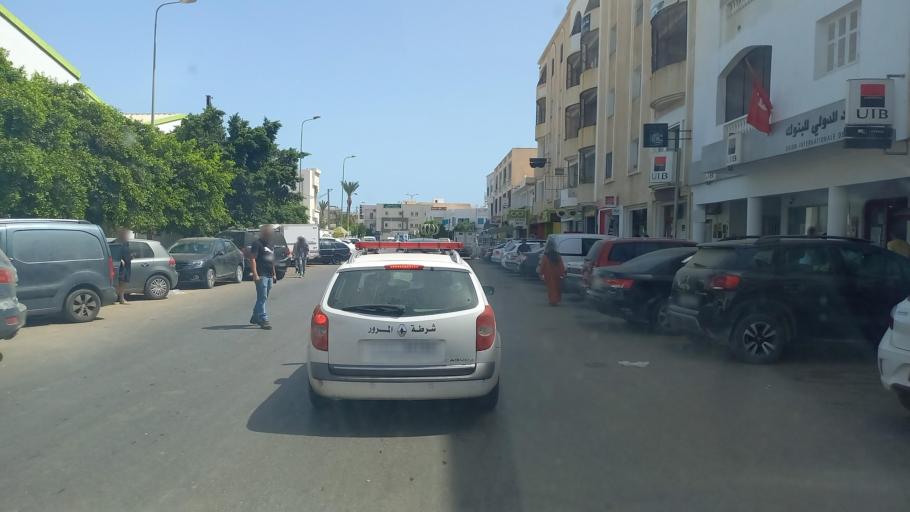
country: TN
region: Madanin
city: Zarzis
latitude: 33.5016
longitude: 11.1051
